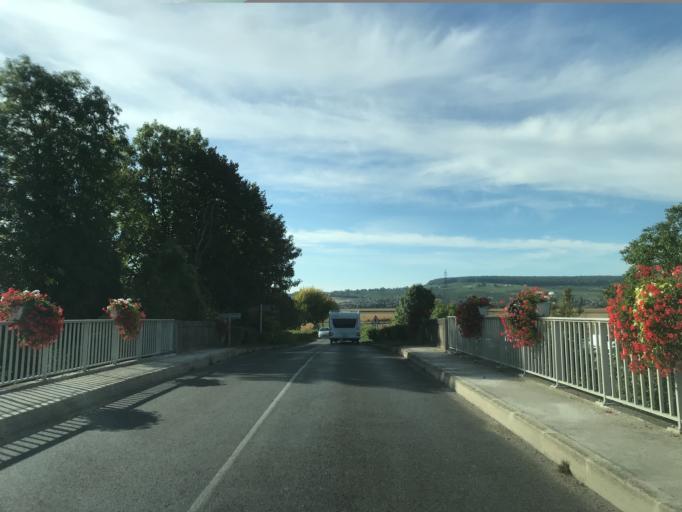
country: FR
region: Champagne-Ardenne
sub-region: Departement de la Marne
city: Mardeuil
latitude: 49.0715
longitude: 3.9311
